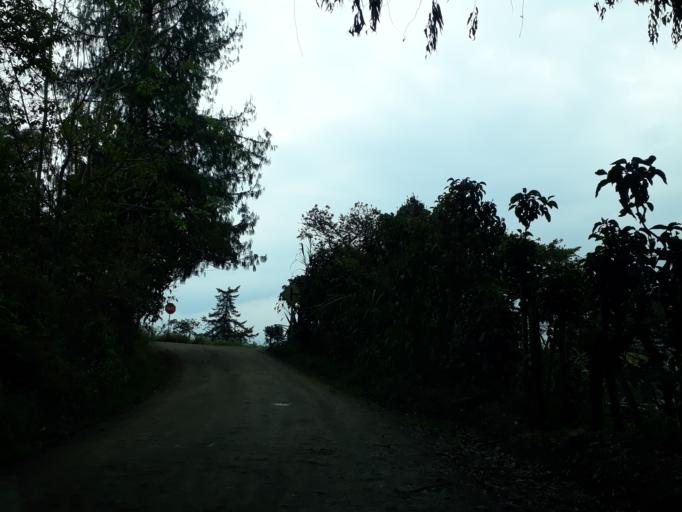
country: CO
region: Cundinamarca
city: Manta
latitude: 5.0028
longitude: -73.5478
